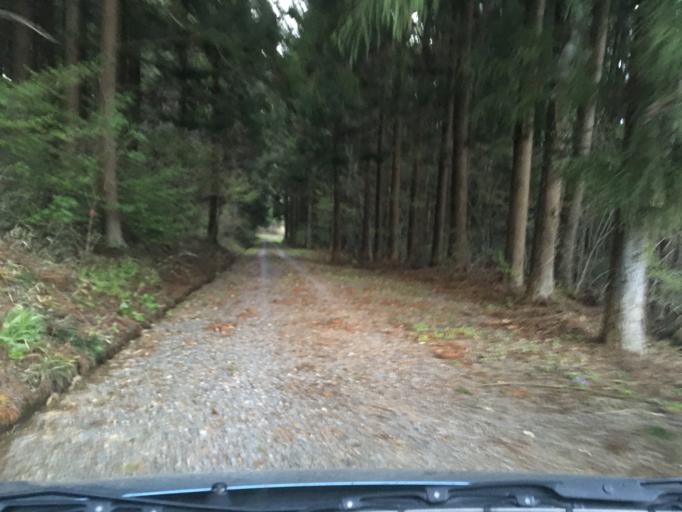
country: JP
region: Iwate
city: Ichinoseki
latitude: 38.9601
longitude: 141.2044
